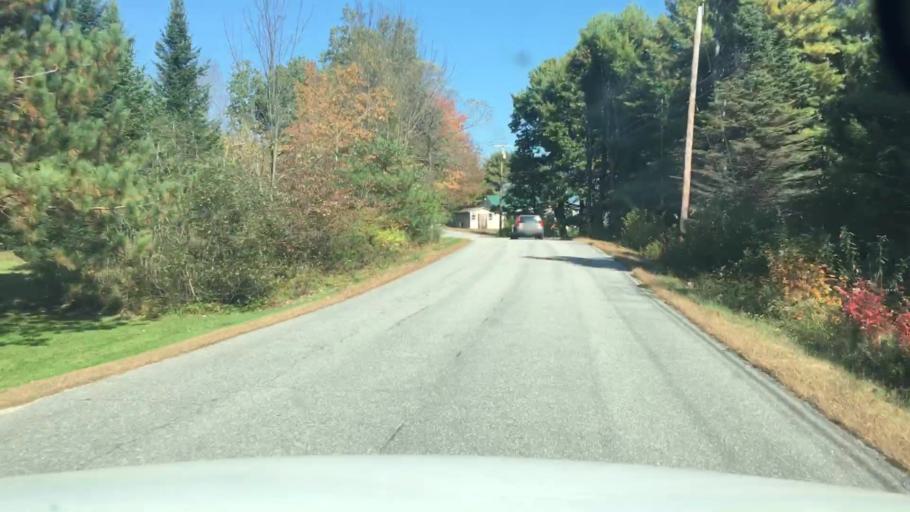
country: US
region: Maine
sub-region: Androscoggin County
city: Lisbon Falls
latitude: 44.0309
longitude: -69.9869
